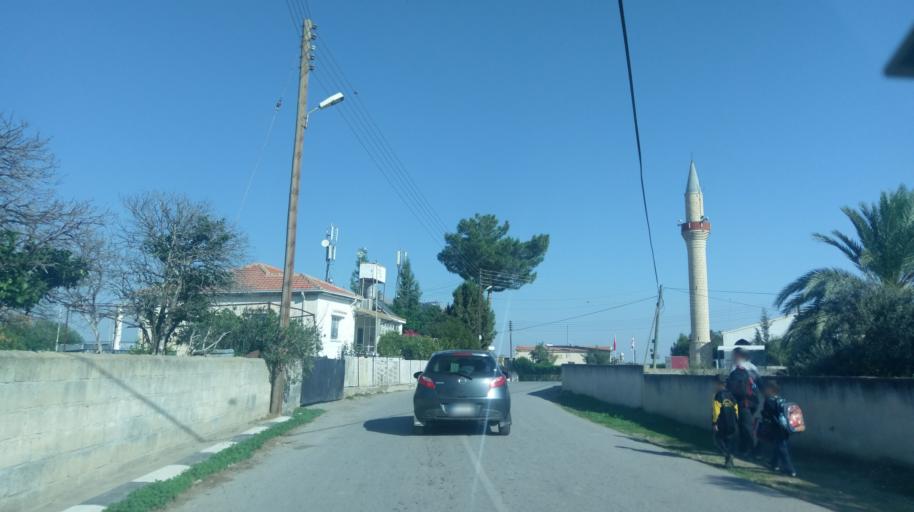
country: CY
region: Larnaka
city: Athienou
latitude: 35.1747
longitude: 33.5486
